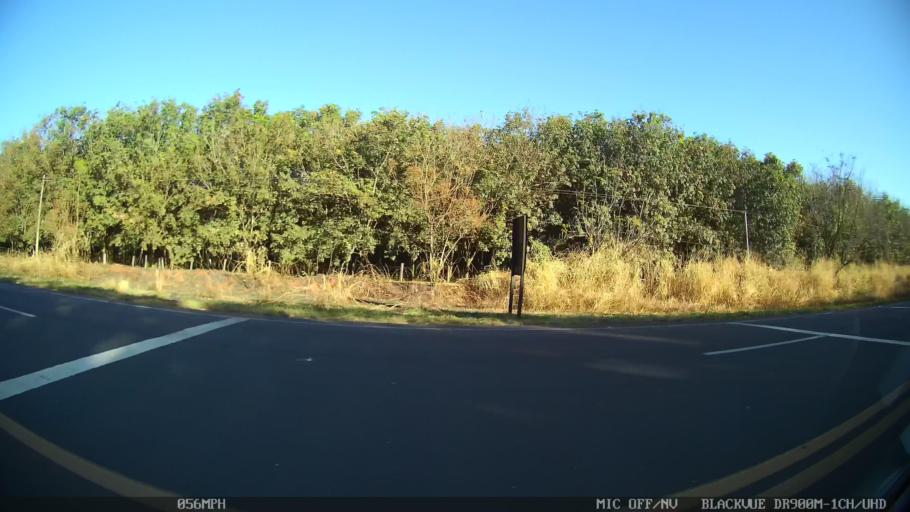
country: BR
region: Sao Paulo
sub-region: Guapiacu
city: Guapiacu
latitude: -20.7623
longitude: -49.1822
